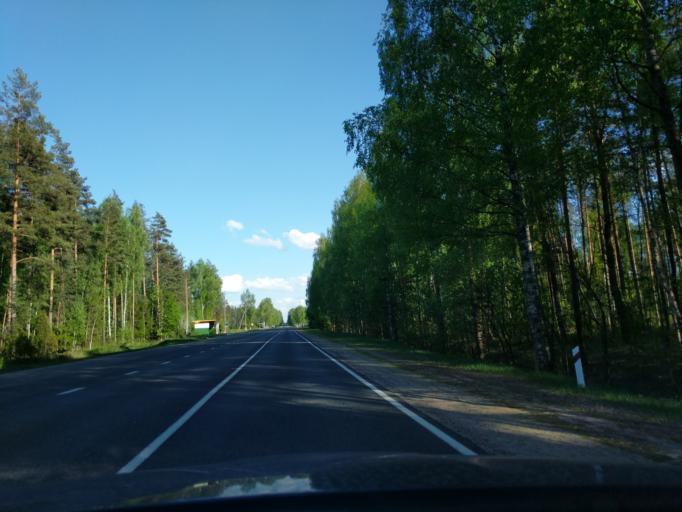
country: BY
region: Minsk
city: Myadzyel
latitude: 54.8165
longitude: 26.9673
